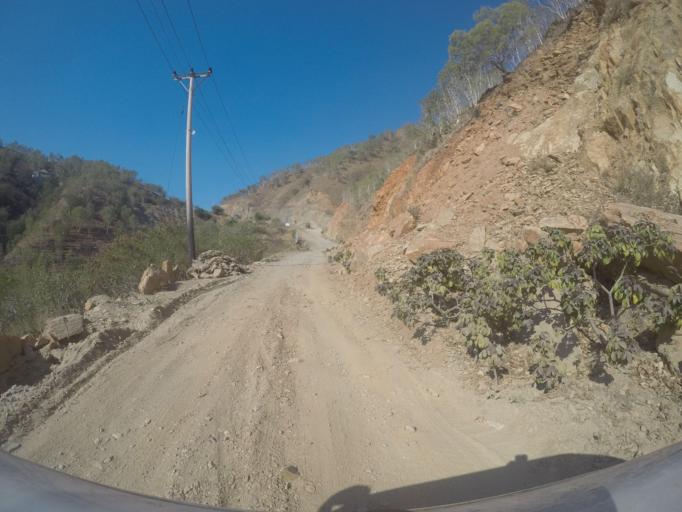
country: TL
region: Dili
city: Dili
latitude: -8.5322
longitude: 125.6186
